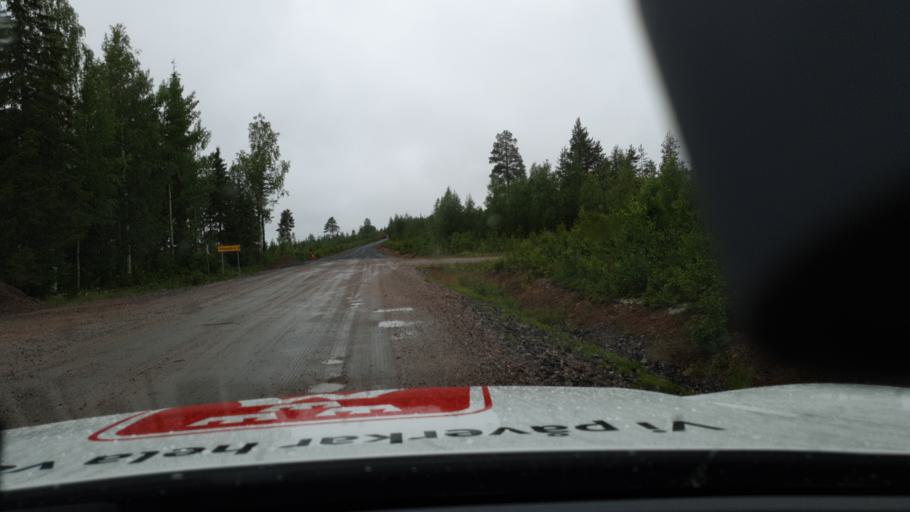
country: SE
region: Norrbotten
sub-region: Overtornea Kommun
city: OEvertornea
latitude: 66.5864
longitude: 23.3228
